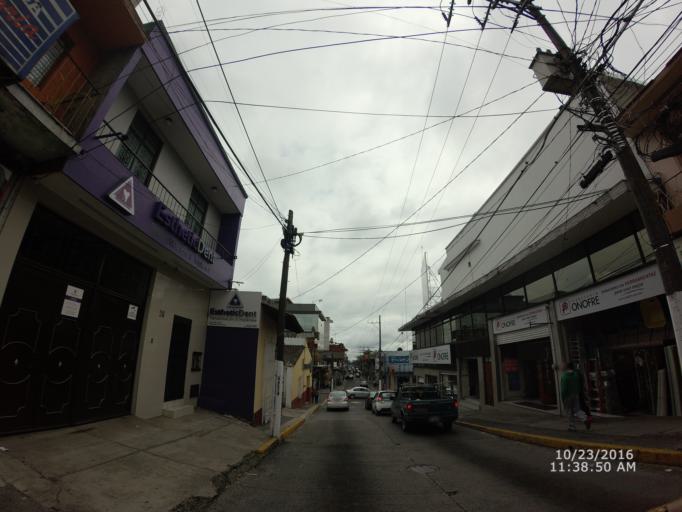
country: MX
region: Veracruz
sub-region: Xalapa
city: Xalapa de Enriquez
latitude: 19.5328
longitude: -96.9249
